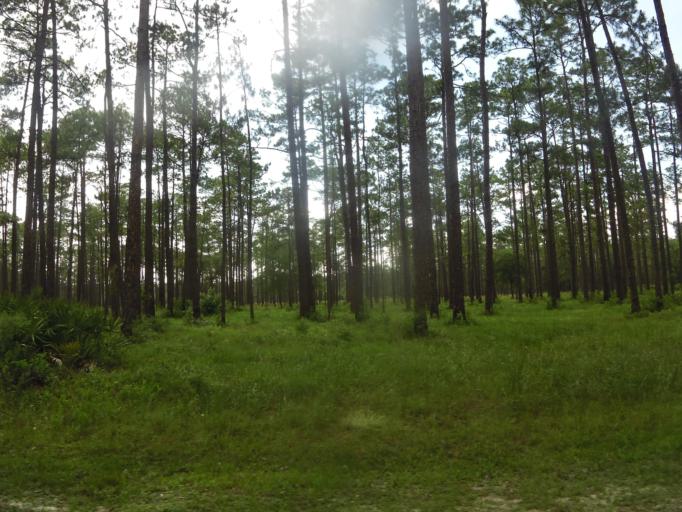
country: US
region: Florida
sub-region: Union County
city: Lake Butler
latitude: 30.2166
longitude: -82.3864
